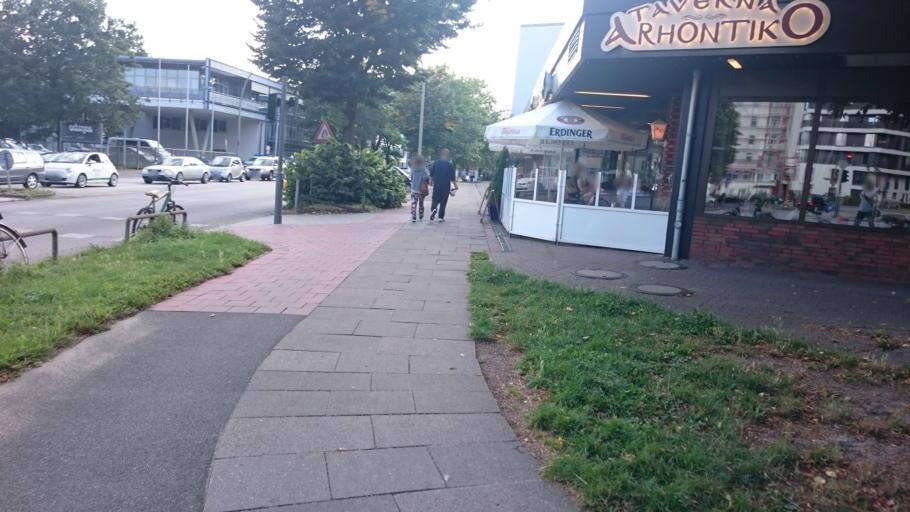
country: DE
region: Hamburg
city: Hamburg-Nord
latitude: 53.5860
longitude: 9.9674
